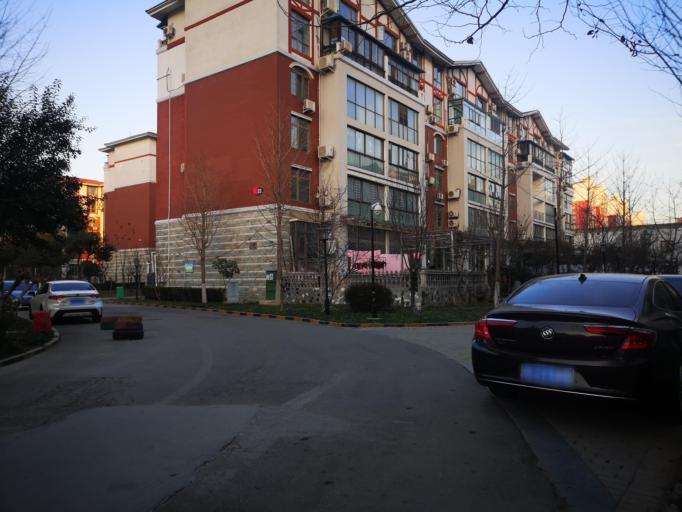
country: CN
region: Henan Sheng
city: Zhongyuanlu
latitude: 35.7614
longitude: 115.0769
